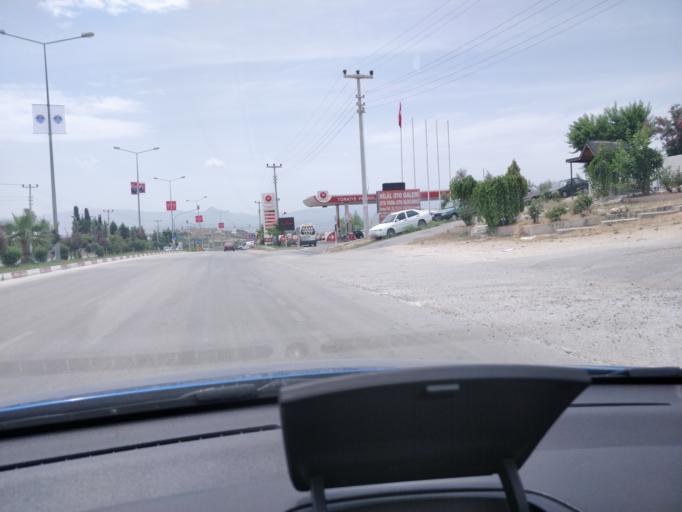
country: TR
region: Mersin
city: Mut
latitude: 36.6304
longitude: 33.4473
